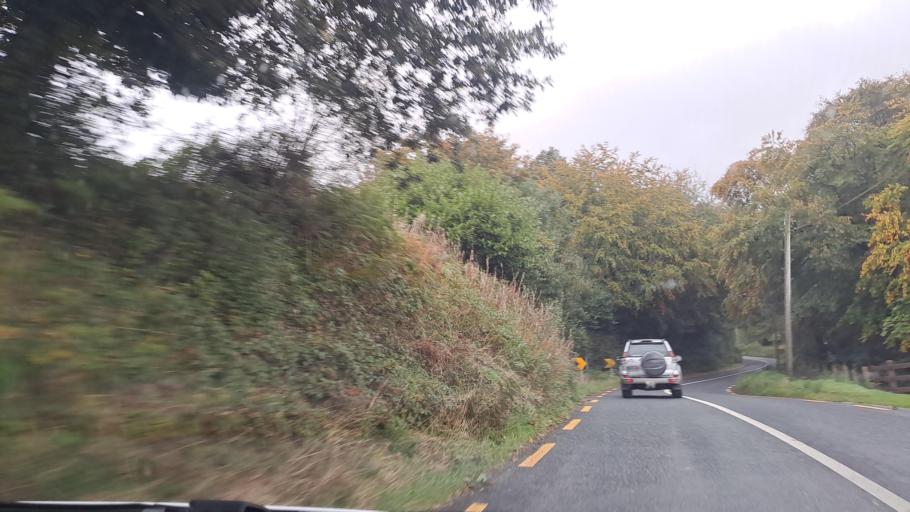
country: IE
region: Ulster
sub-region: An Cabhan
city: Bailieborough
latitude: 53.9382
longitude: -7.0198
